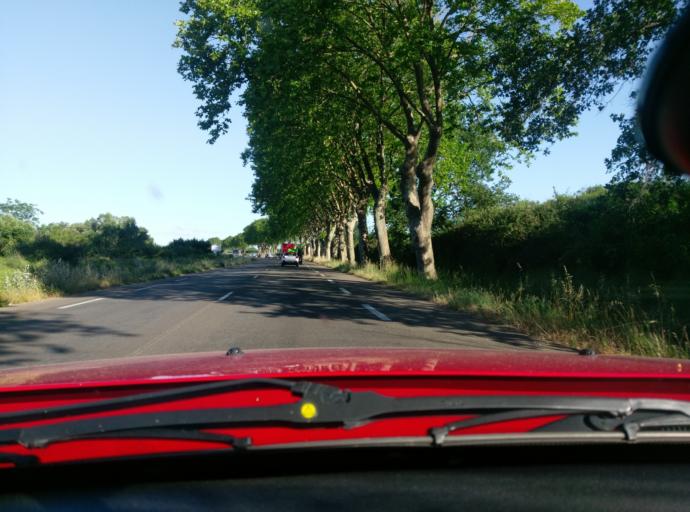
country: FR
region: Languedoc-Roussillon
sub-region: Departement du Gard
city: Uzes
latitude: 43.9830
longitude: 4.4647
